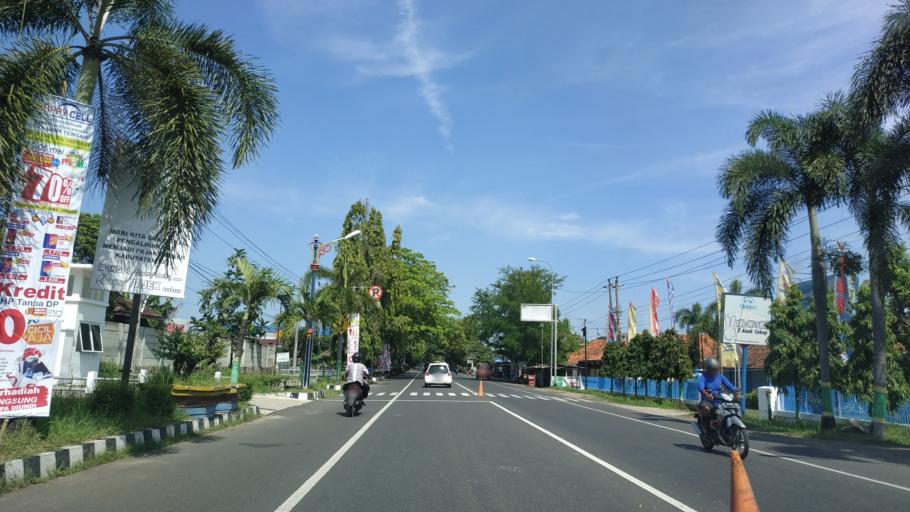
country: ID
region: Central Java
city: Baran
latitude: -6.7517
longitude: 111.0536
